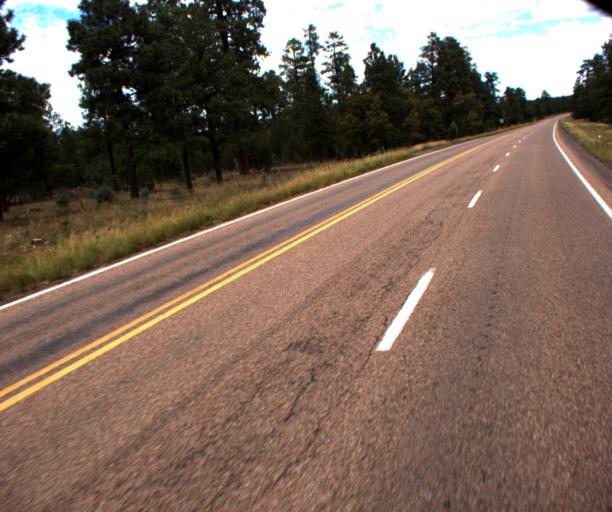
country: US
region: Arizona
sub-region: Navajo County
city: Heber-Overgaard
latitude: 34.3970
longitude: -110.6708
